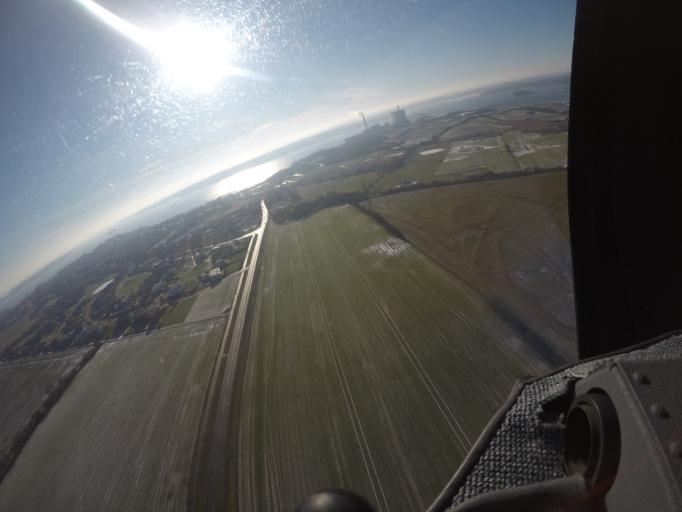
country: DK
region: South Denmark
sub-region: Fredericia Kommune
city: Taulov
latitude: 55.5252
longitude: 9.6225
